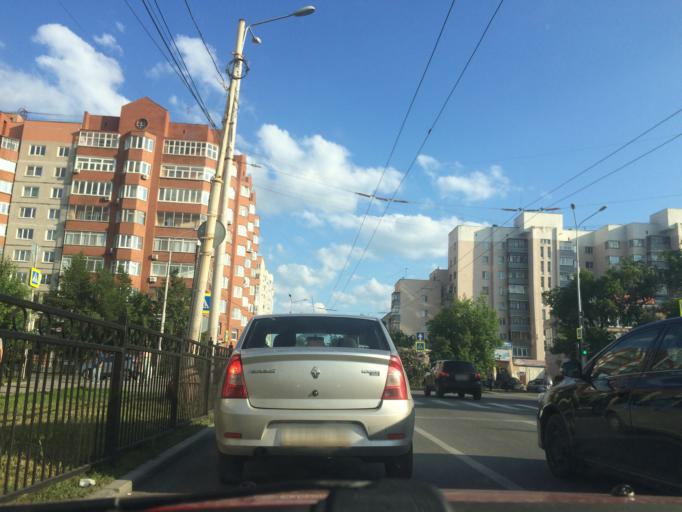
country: RU
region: Sverdlovsk
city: Yekaterinburg
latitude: 56.8166
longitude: 60.6139
